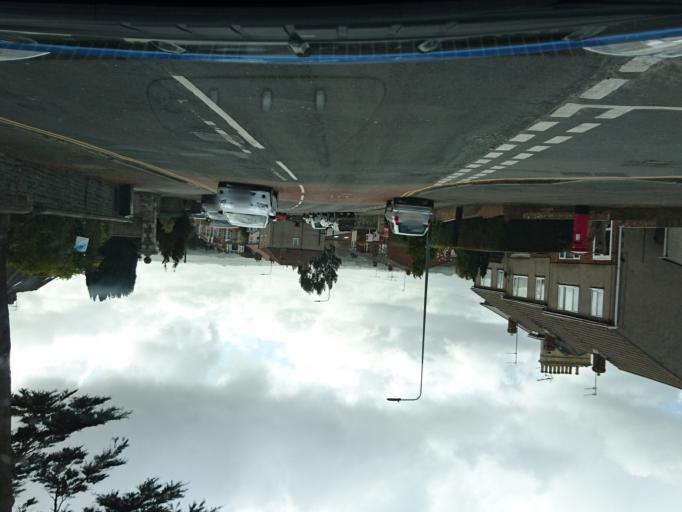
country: GB
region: England
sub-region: South Gloucestershire
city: Kingswood
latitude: 51.4611
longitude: -2.4904
